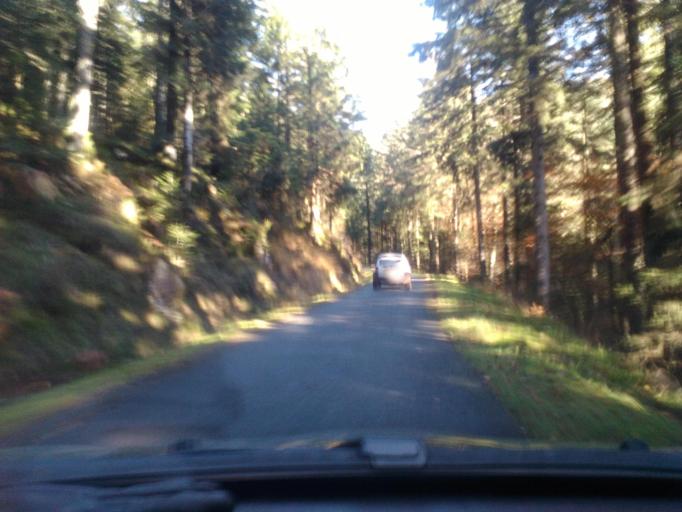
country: FR
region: Lorraine
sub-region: Departement des Vosges
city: Senones
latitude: 48.4654
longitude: 7.0697
